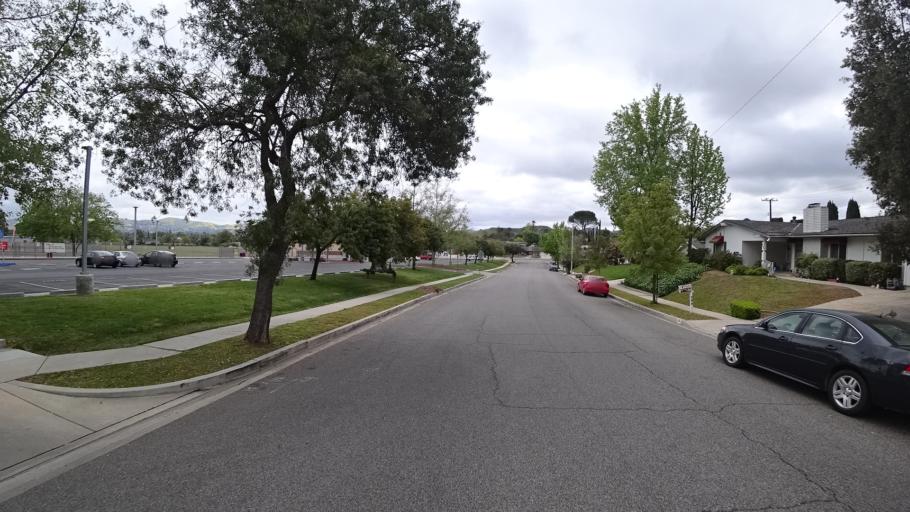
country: US
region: California
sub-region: Ventura County
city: Thousand Oaks
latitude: 34.1975
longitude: -118.8848
